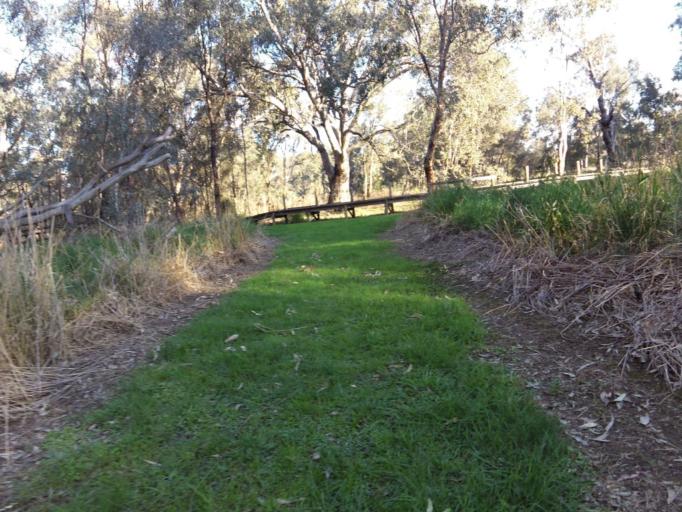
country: AU
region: Victoria
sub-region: Murrindindi
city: Alexandra
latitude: -37.2063
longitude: 145.4272
